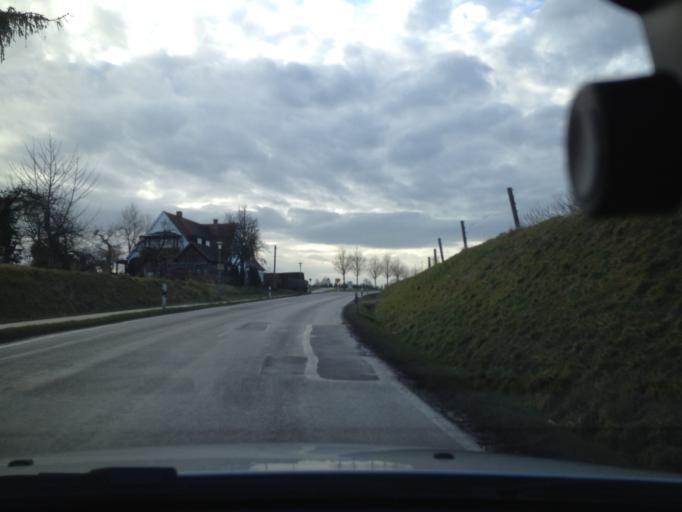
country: DE
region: Bavaria
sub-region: Swabia
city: Langerringen
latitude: 48.1358
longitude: 10.7531
